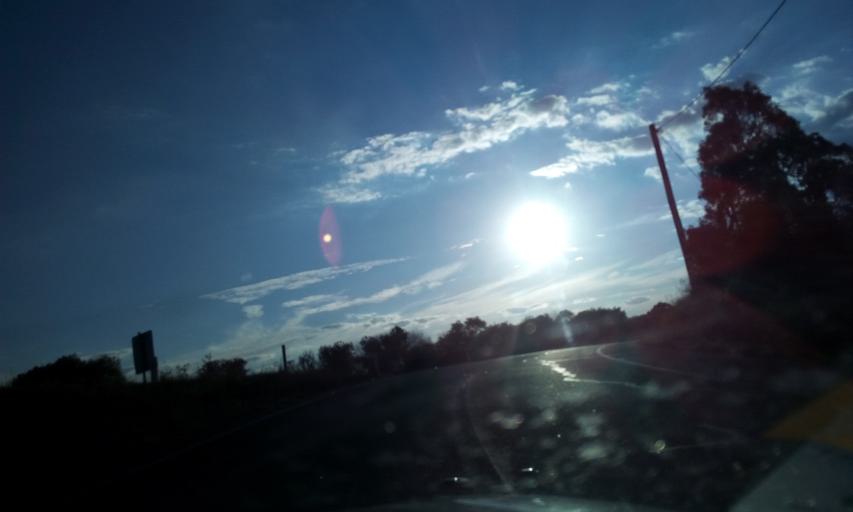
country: AU
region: New South Wales
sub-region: Wollondilly
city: Douglas Park
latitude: -34.1648
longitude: 150.7189
